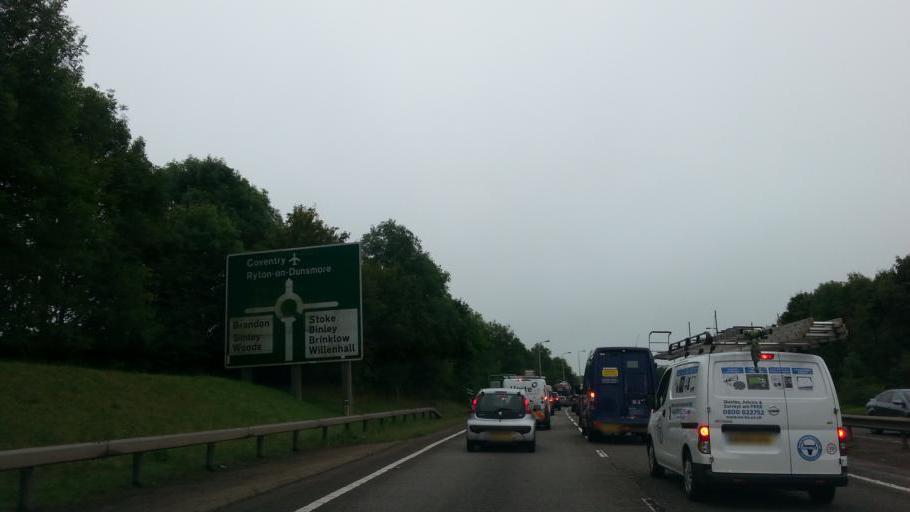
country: GB
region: England
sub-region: Warwickshire
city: Ryton on Dunsmore
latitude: 52.3981
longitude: -1.4305
